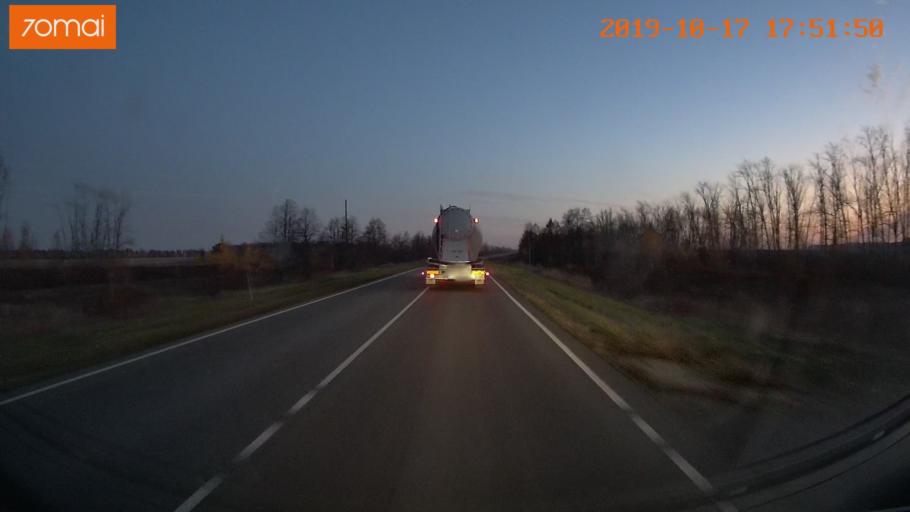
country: RU
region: Tula
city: Kurkino
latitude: 53.6426
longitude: 38.6840
